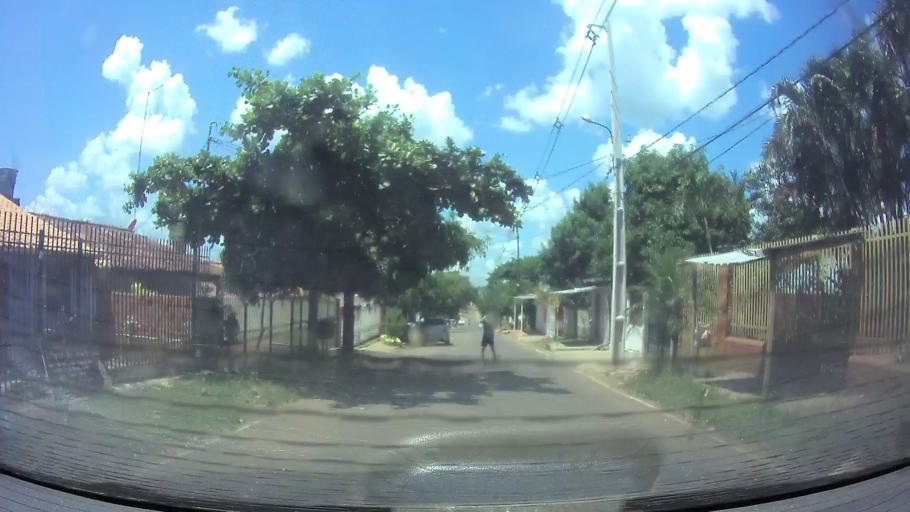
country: PY
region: Central
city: Limpio
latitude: -25.1525
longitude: -57.4510
